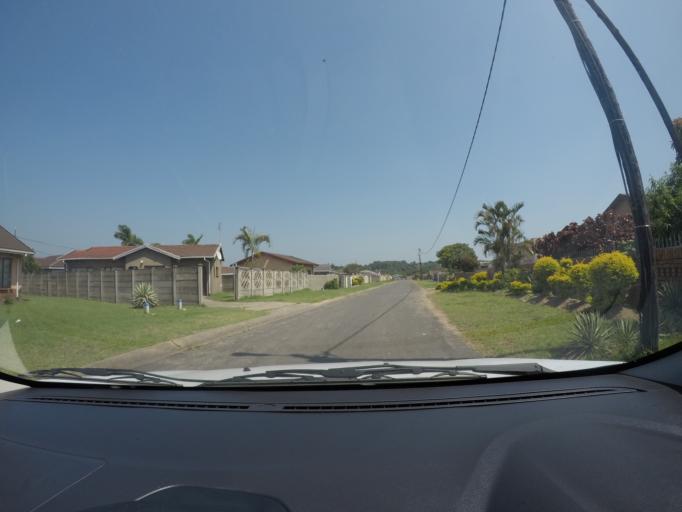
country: ZA
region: KwaZulu-Natal
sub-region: uThungulu District Municipality
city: eSikhawini
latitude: -28.8620
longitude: 31.9197
